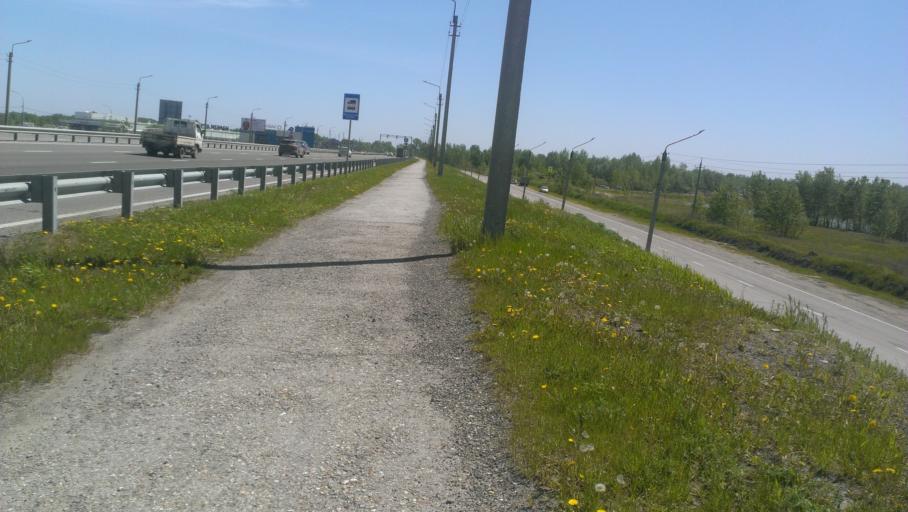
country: RU
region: Altai Krai
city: Zaton
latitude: 53.3182
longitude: 83.8186
